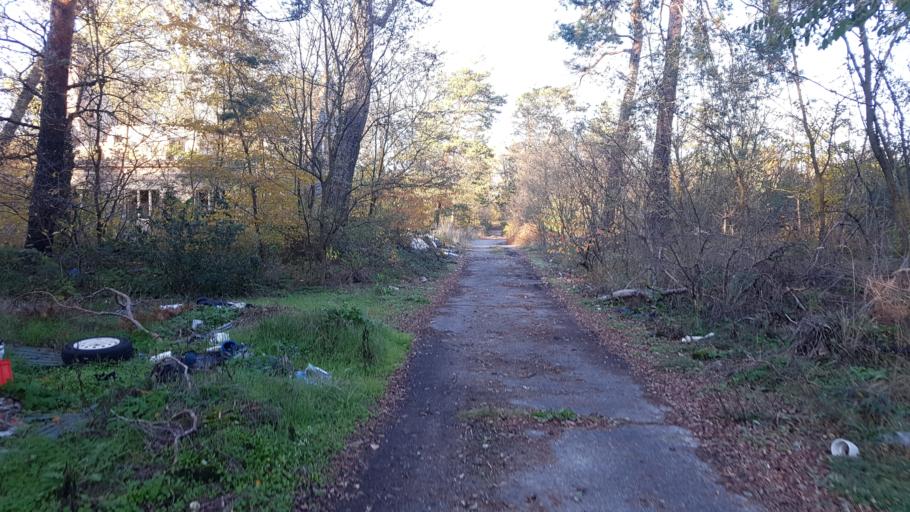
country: DE
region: Brandenburg
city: Finsterwalde
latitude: 51.5997
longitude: 13.7442
